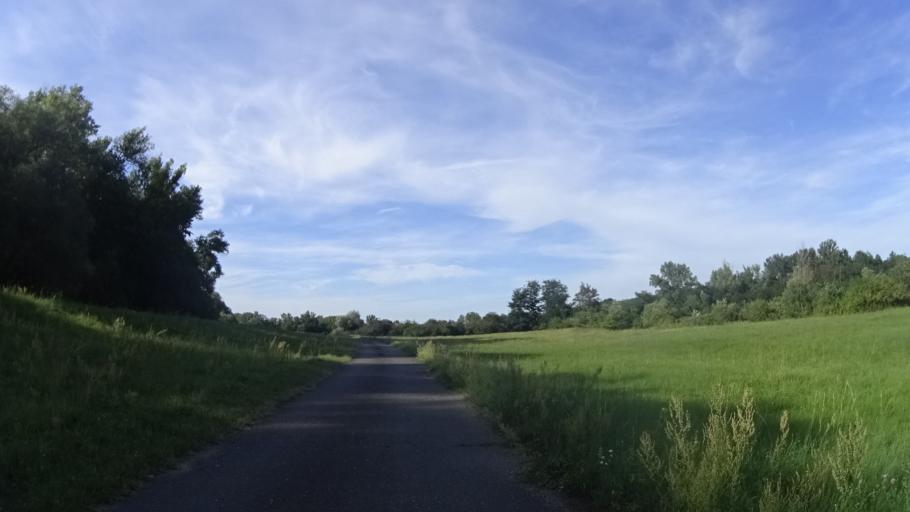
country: AT
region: Lower Austria
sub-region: Politischer Bezirk Ganserndorf
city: Drosing
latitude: 48.5481
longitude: 16.9631
